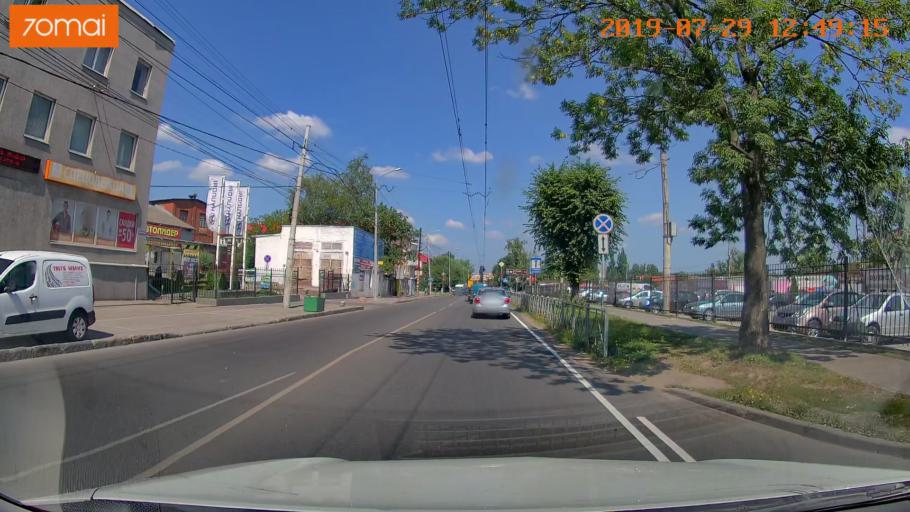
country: RU
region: Kaliningrad
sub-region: Gorod Kaliningrad
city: Kaliningrad
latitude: 54.6841
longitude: 20.5338
